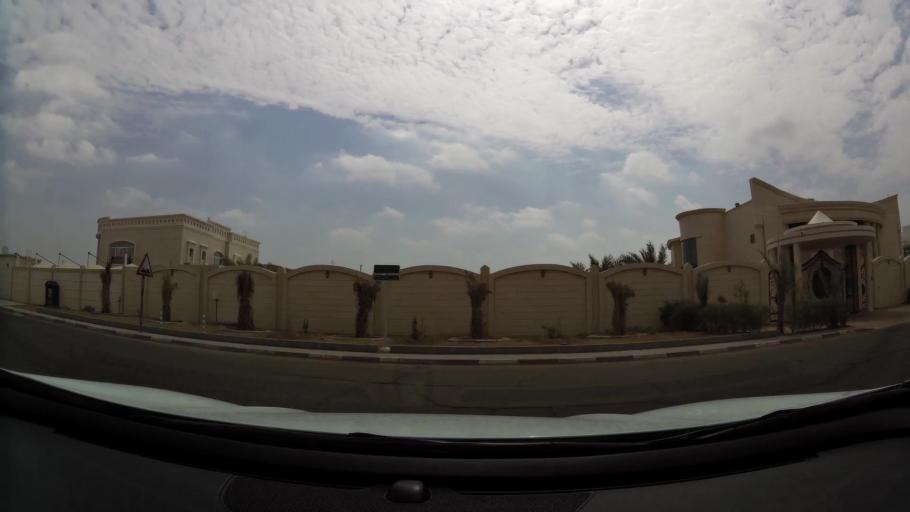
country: AE
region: Abu Dhabi
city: Al Ain
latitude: 24.1998
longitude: 55.7913
